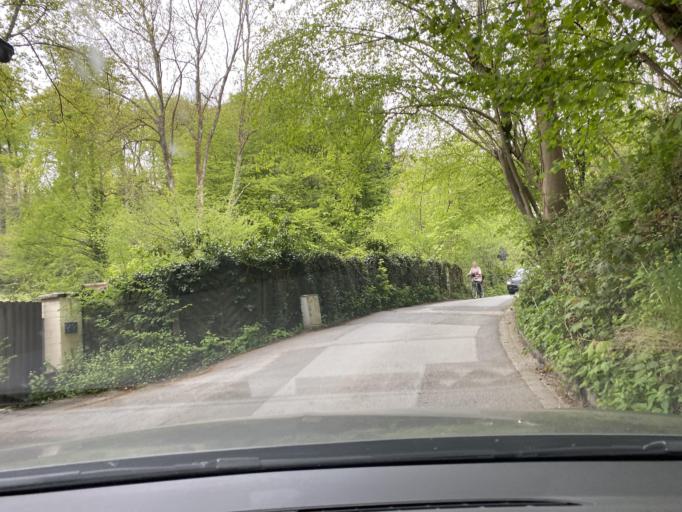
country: DE
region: North Rhine-Westphalia
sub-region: Regierungsbezirk Dusseldorf
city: Ratingen
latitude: 51.3182
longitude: 6.9068
